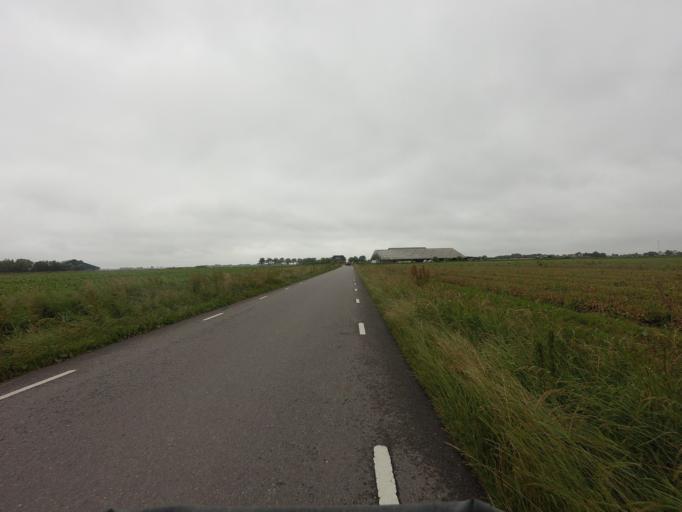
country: NL
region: North Holland
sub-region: Gemeente Schagen
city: Schagen
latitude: 52.7760
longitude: 4.8672
